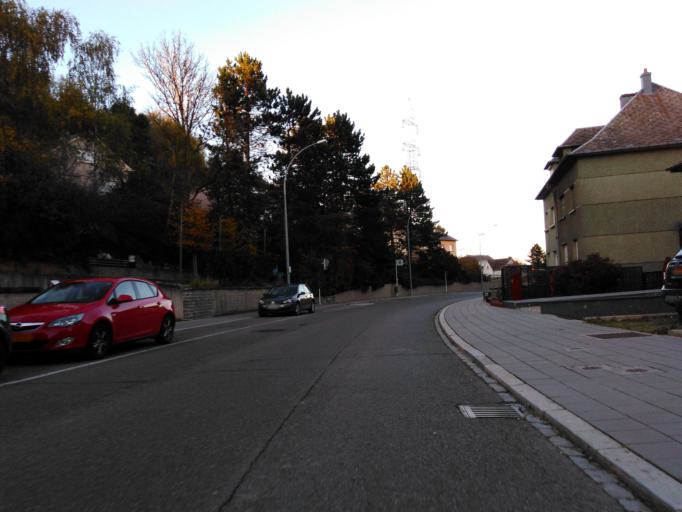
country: LU
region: Luxembourg
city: Belvaux
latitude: 49.5178
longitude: 5.9361
